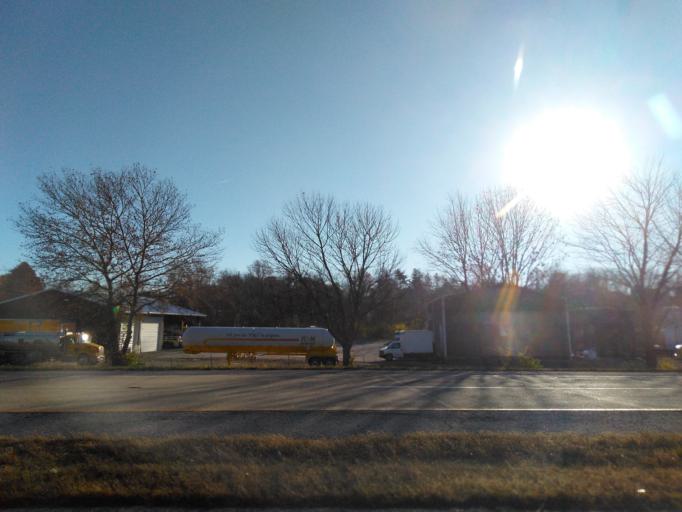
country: US
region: Illinois
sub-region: Monroe County
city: Columbia
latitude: 38.4776
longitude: -90.2238
